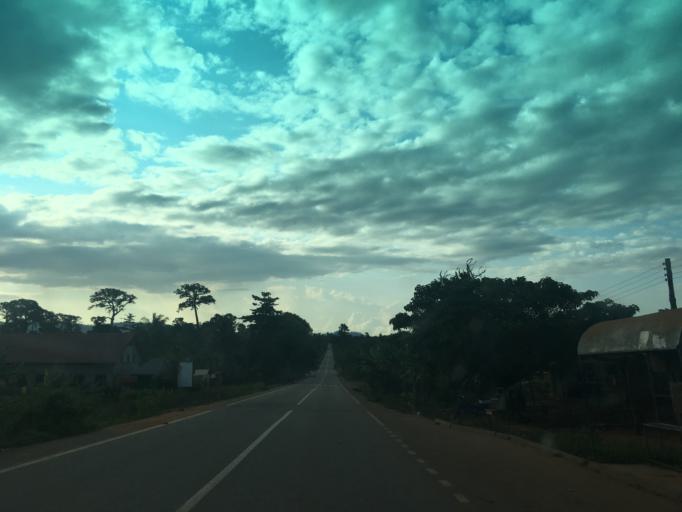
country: GH
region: Western
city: Bibiani
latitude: 6.3555
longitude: -2.2818
